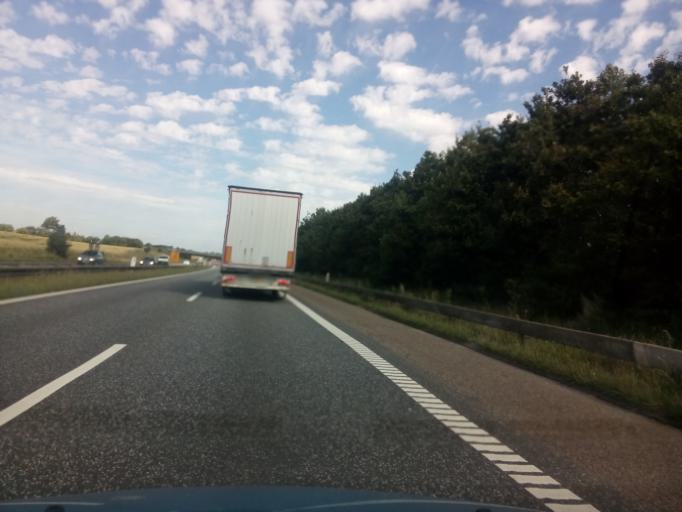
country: DK
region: Central Jutland
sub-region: Favrskov Kommune
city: Hadsten
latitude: 56.3381
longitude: 10.1233
